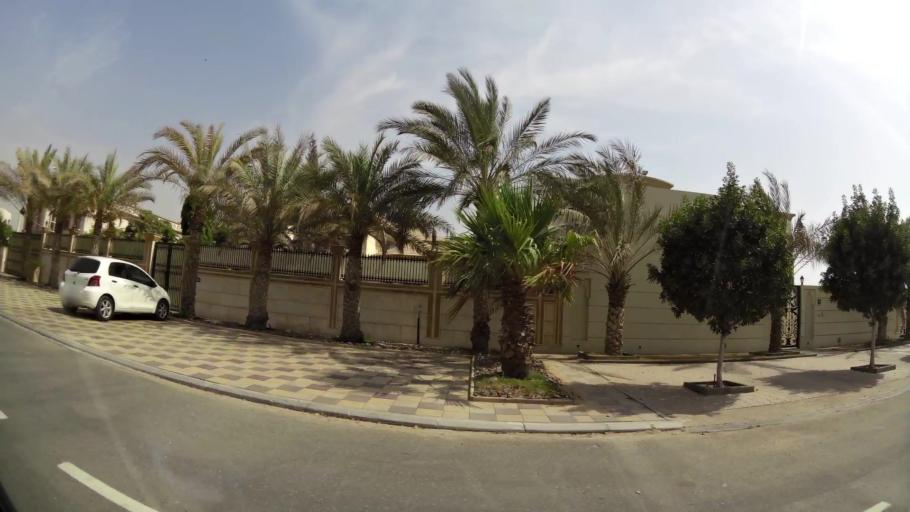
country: AE
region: Ash Shariqah
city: Sharjah
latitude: 25.2492
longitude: 55.4482
